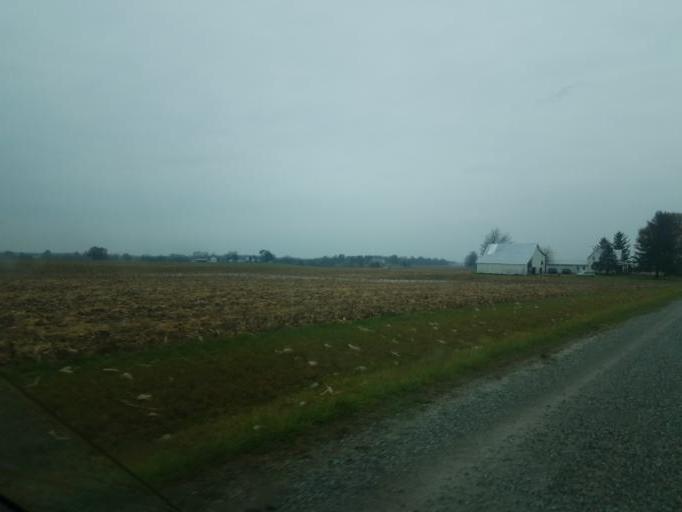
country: US
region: Ohio
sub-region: Knox County
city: Centerburg
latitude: 40.2380
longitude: -82.7233
